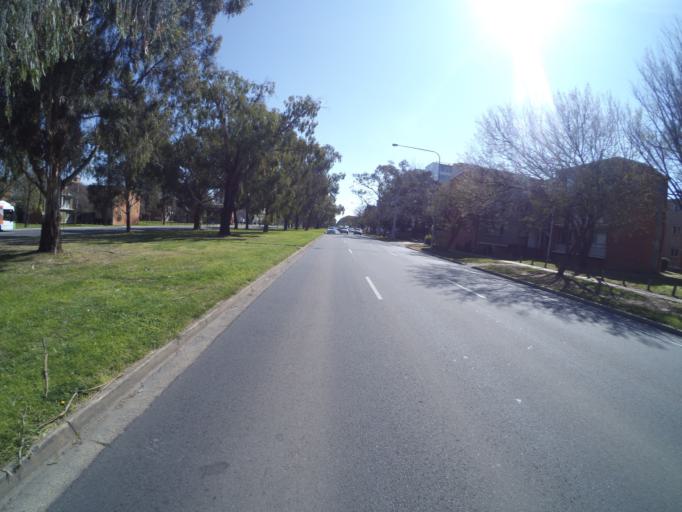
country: AU
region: Australian Capital Territory
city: Canberra
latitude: -35.2678
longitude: 149.1312
